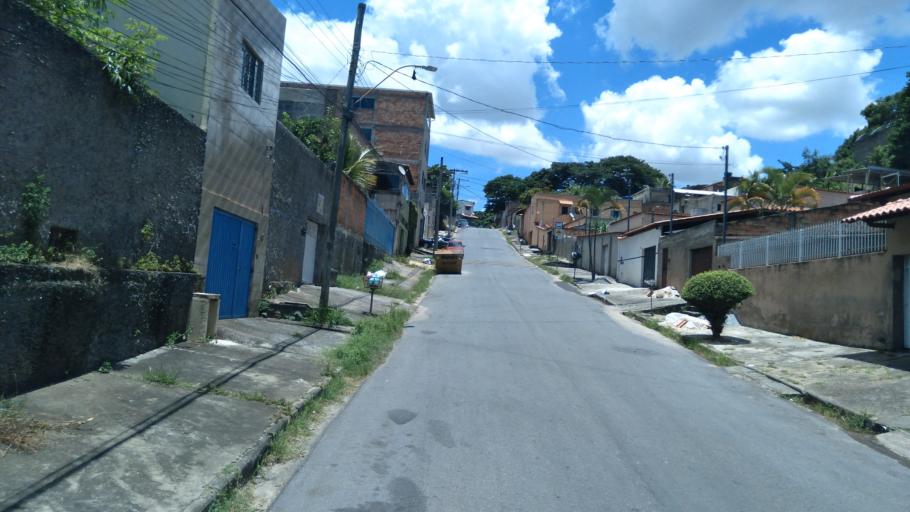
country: BR
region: Minas Gerais
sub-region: Santa Luzia
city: Santa Luzia
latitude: -19.8394
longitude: -43.8939
